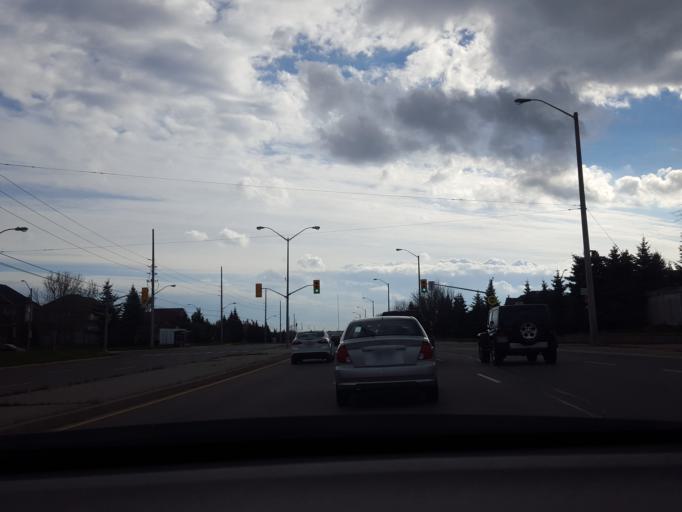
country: CA
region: Ontario
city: Brampton
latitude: 43.6251
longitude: -79.7431
